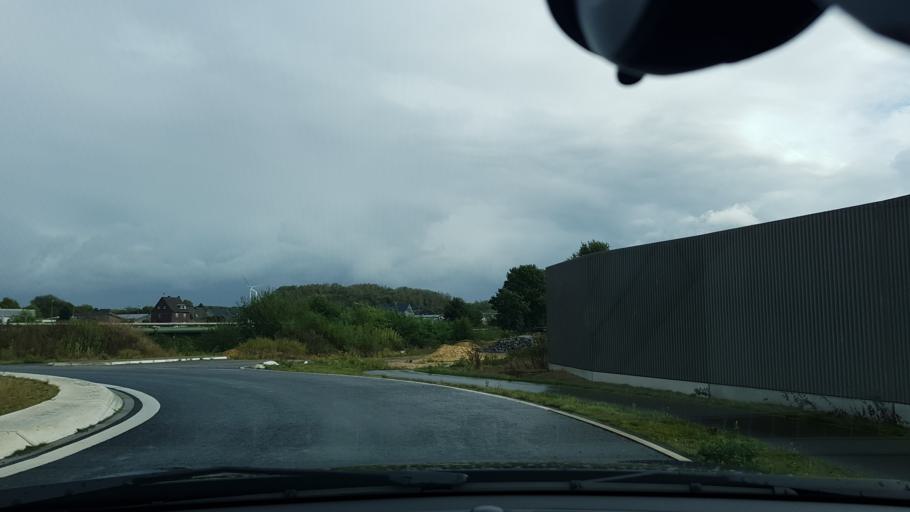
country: DE
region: North Rhine-Westphalia
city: Huckelhoven
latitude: 51.0626
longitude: 6.2010
